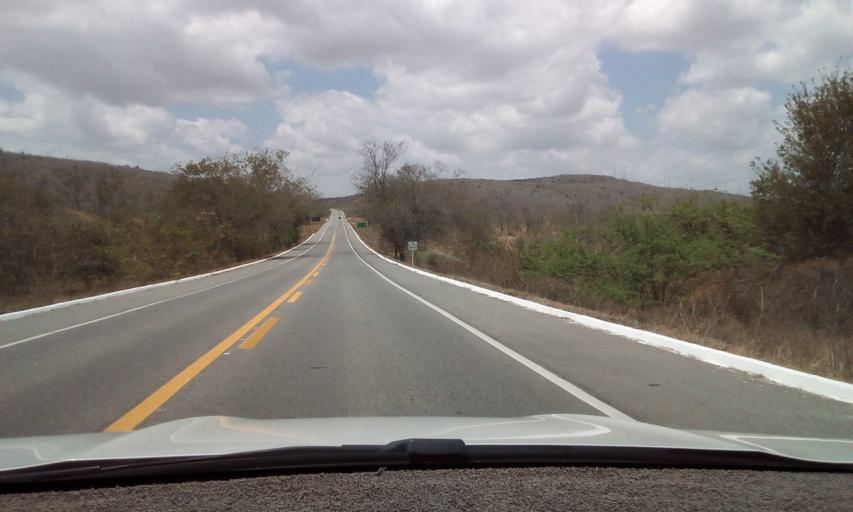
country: BR
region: Paraiba
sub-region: Boqueirao
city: Boqueirao
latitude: -7.6614
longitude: -36.0799
